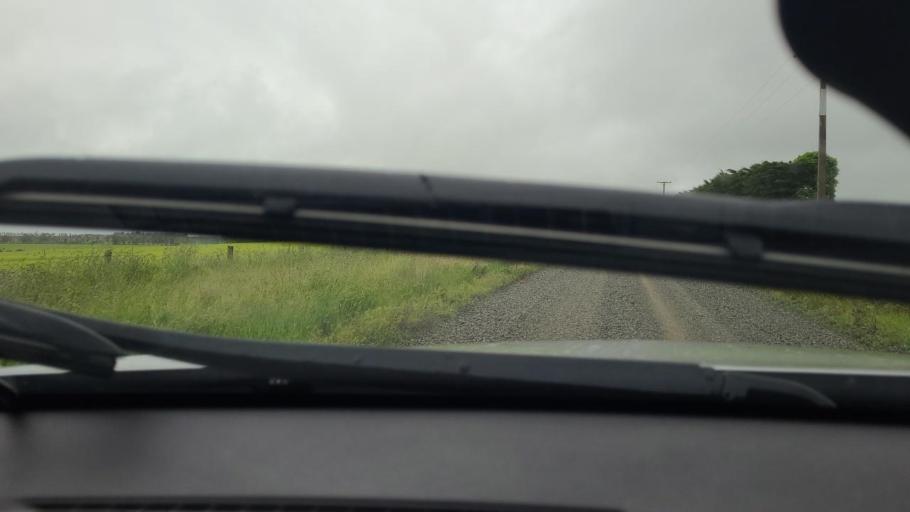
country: NZ
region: Southland
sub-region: Southland District
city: Riverton
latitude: -46.1895
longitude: 168.1015
